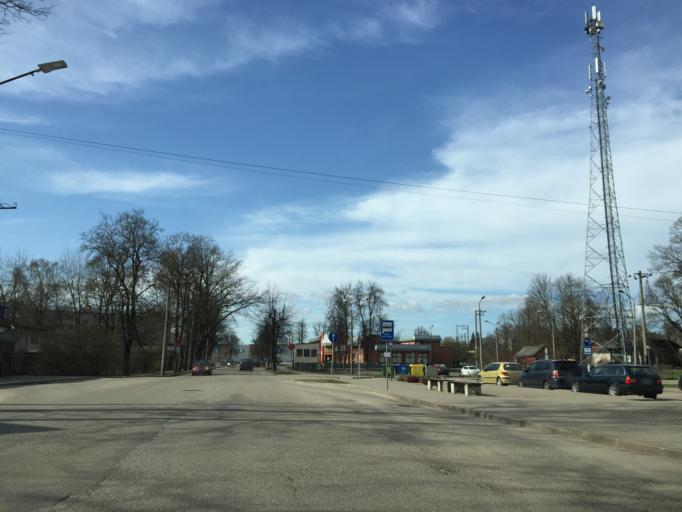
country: LV
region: Ogre
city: Ogre
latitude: 56.8149
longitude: 24.6014
